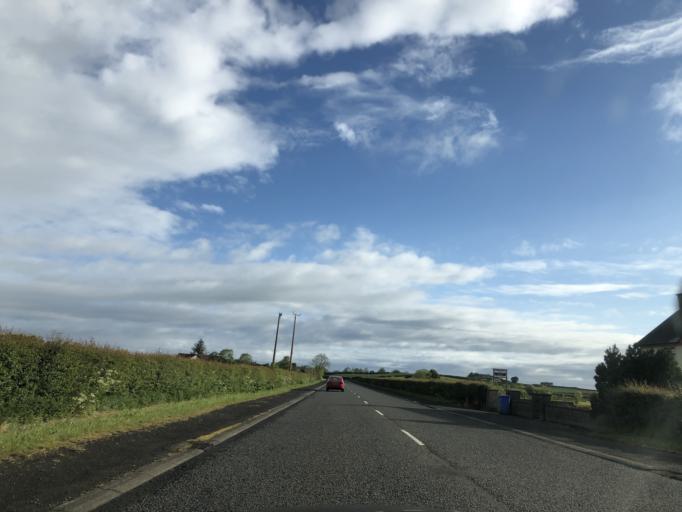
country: GB
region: Northern Ireland
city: Bushmills
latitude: 55.1620
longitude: -6.5749
